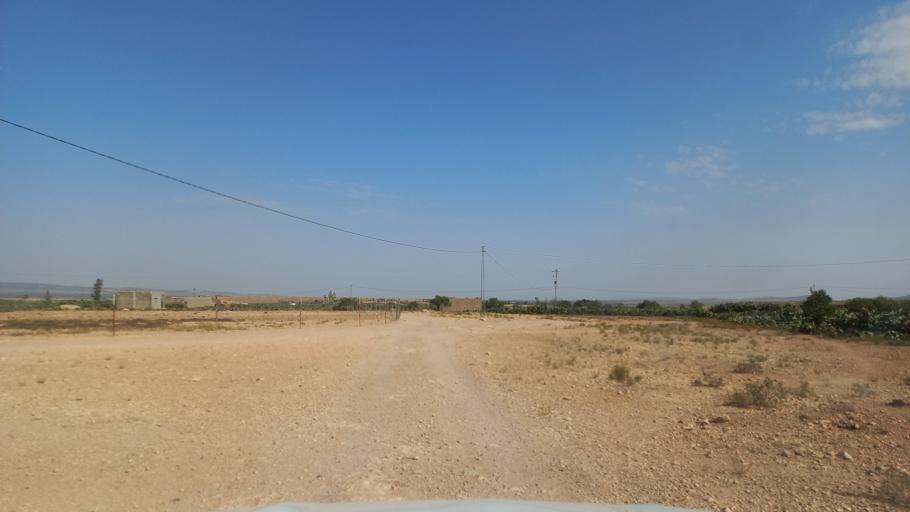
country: TN
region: Al Qasrayn
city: Kasserine
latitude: 35.2835
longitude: 8.9454
